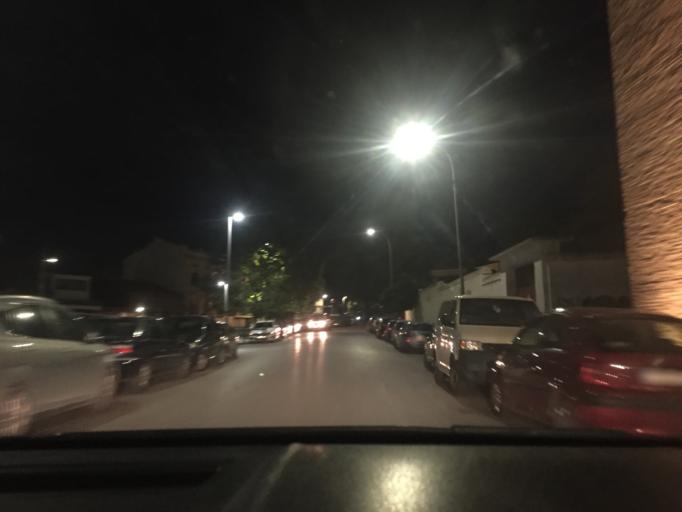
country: ES
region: Andalusia
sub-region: Provincia de Jaen
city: Jaen
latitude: 37.7677
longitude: -3.7828
